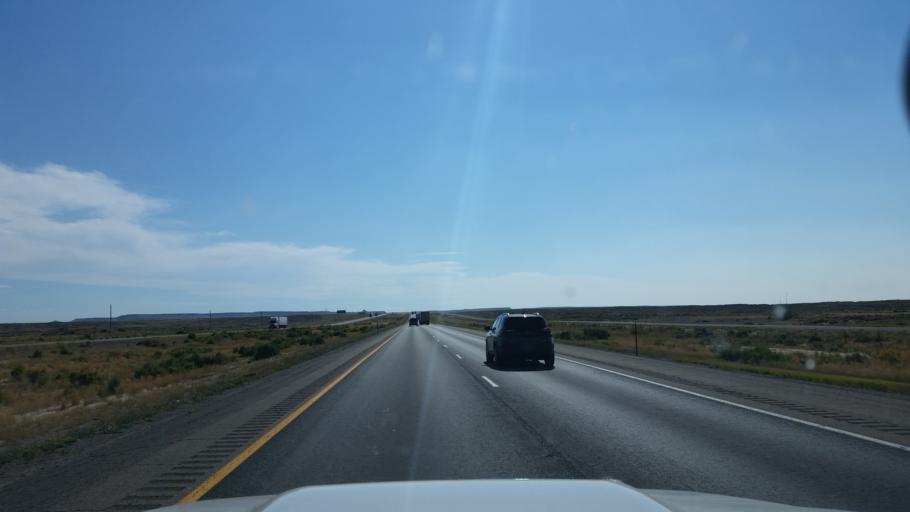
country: US
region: Wyoming
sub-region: Uinta County
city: Lyman
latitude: 41.5315
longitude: -109.9420
